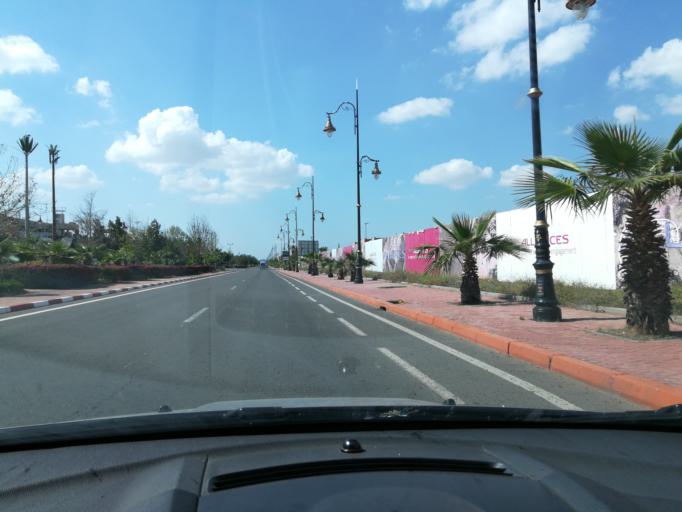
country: MA
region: Marrakech-Tensift-Al Haouz
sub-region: Marrakech
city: Marrakesh
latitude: 31.5853
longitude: -7.9866
